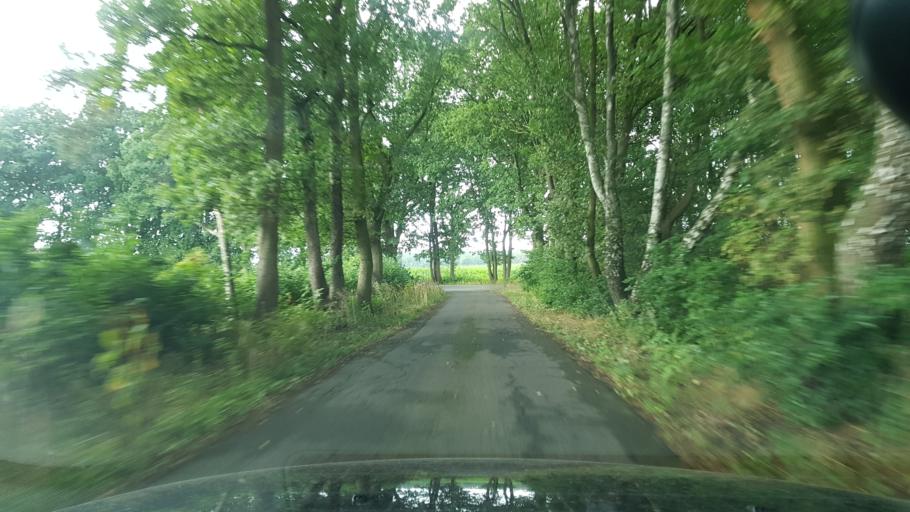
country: DE
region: Lower Saxony
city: Wehrbleck
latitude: 52.6768
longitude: 8.7202
